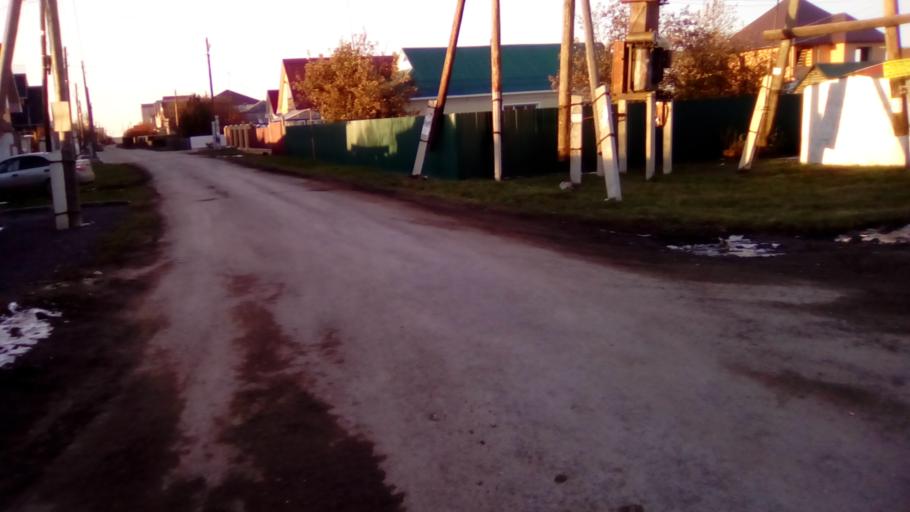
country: RU
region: Tjumen
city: Moskovskiy
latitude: 57.2195
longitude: 65.3669
